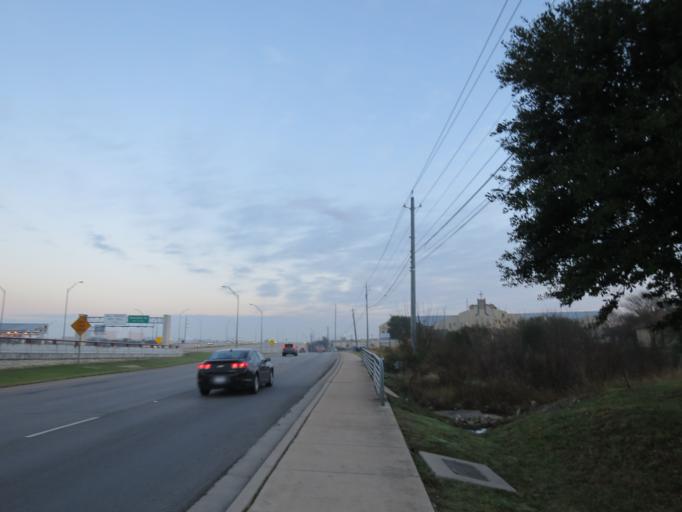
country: US
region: Texas
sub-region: Travis County
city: Wells Branch
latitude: 30.4344
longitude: -97.6988
